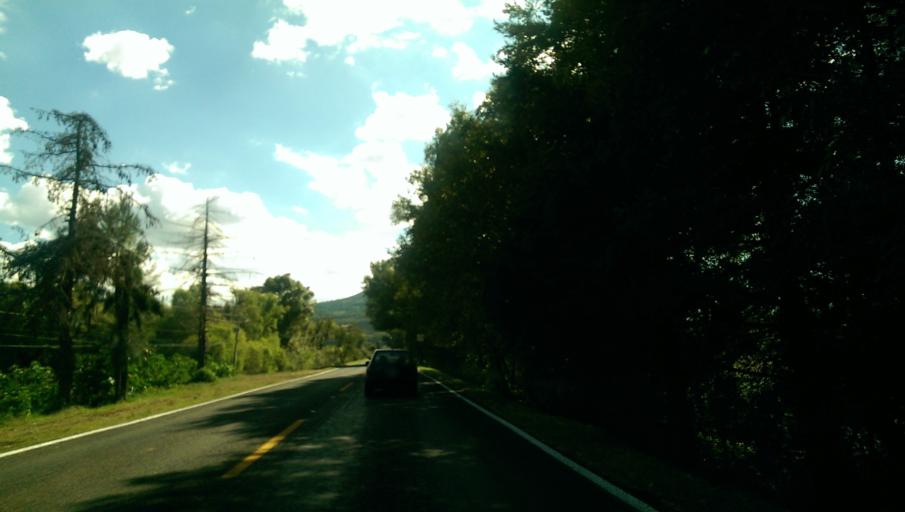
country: MX
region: Michoacan
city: Quiroga
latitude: 19.6481
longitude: -101.5327
